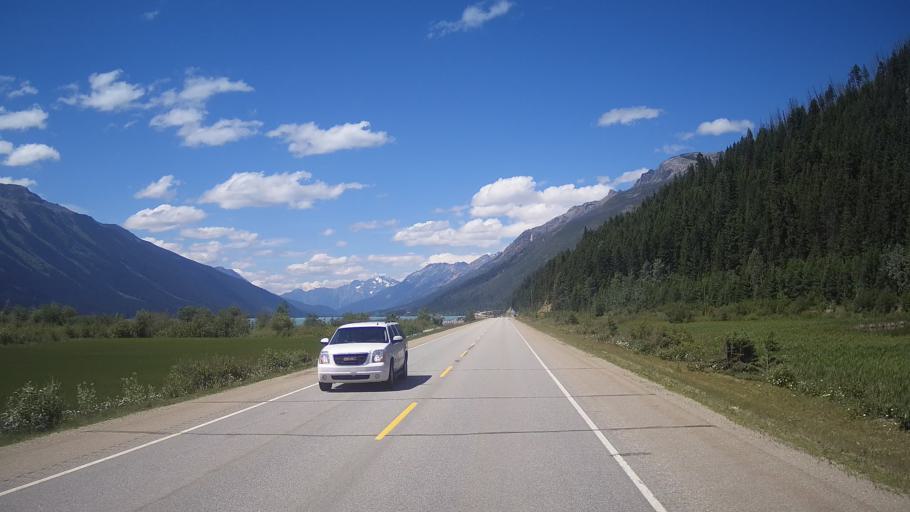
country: CA
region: Alberta
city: Jasper Park Lodge
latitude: 52.9355
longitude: -118.8394
